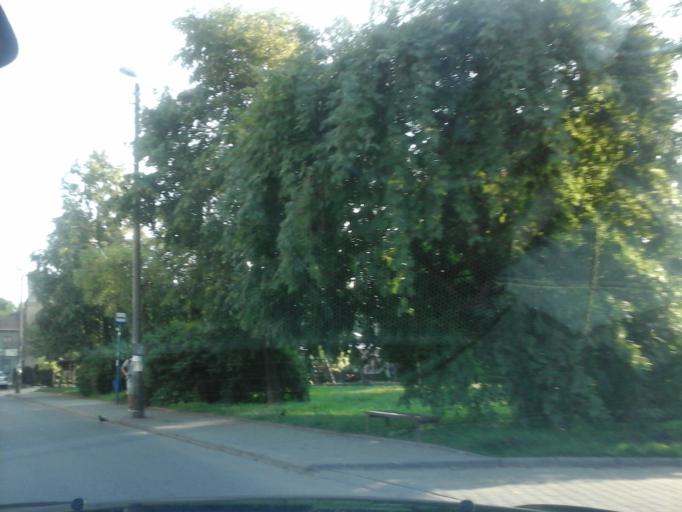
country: PL
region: Lesser Poland Voivodeship
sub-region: Powiat krakowski
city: Skawina
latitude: 49.9767
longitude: 19.8219
